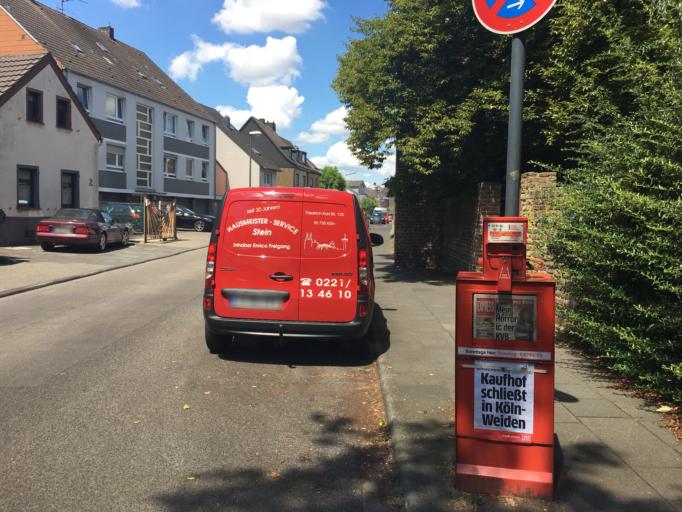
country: DE
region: North Rhine-Westphalia
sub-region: Regierungsbezirk Koln
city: Mengenich
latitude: 50.9807
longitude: 6.8579
